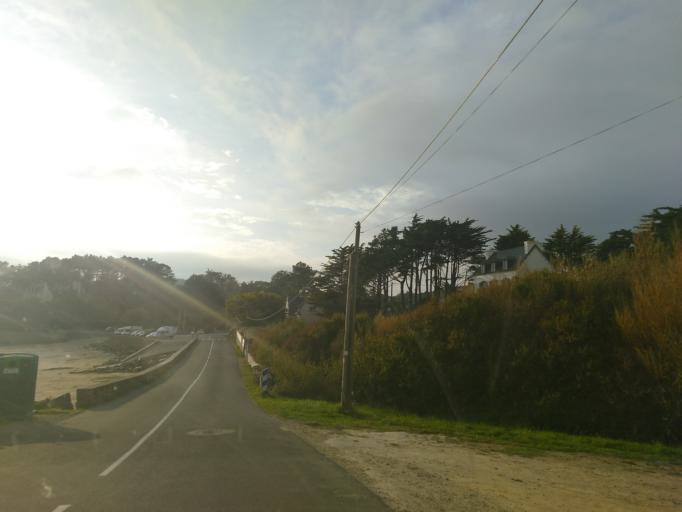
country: FR
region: Brittany
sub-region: Departement du Finistere
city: Crozon
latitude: 48.2389
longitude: -4.4619
